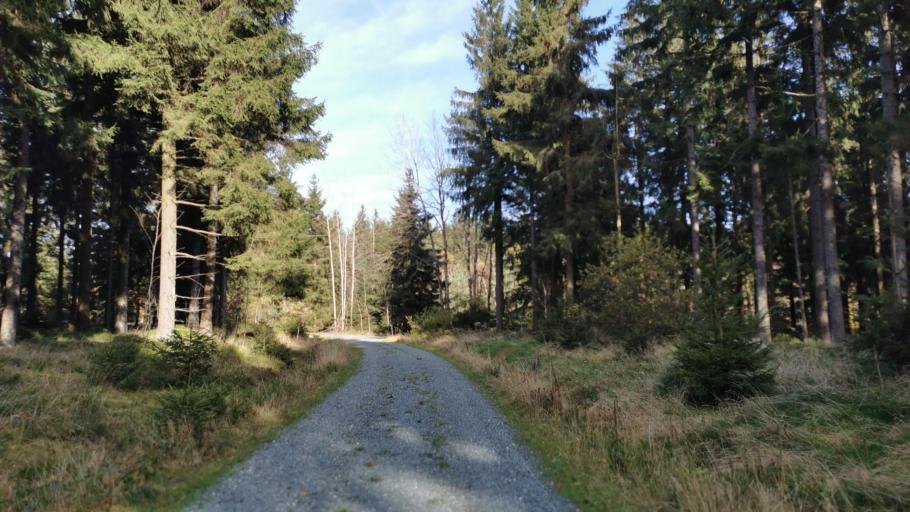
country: DE
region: Bavaria
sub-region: Upper Franconia
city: Tschirn
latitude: 50.4314
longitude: 11.4680
